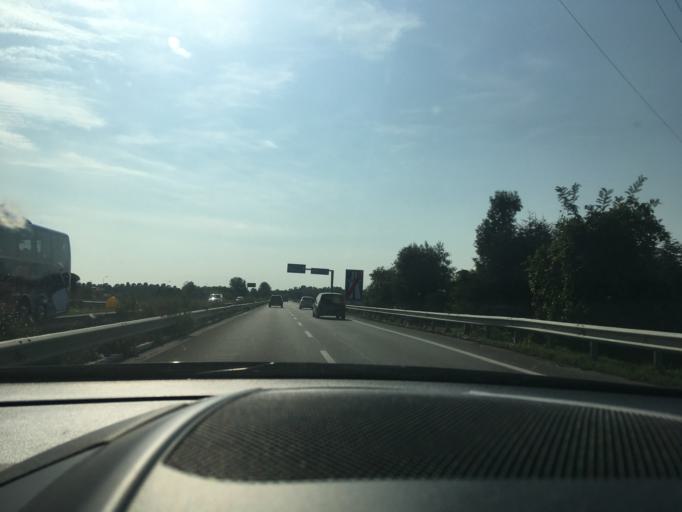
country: IT
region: Emilia-Romagna
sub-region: Provincia di Rimini
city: Bellaria-Igea Marina
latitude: 44.1142
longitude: 12.4777
